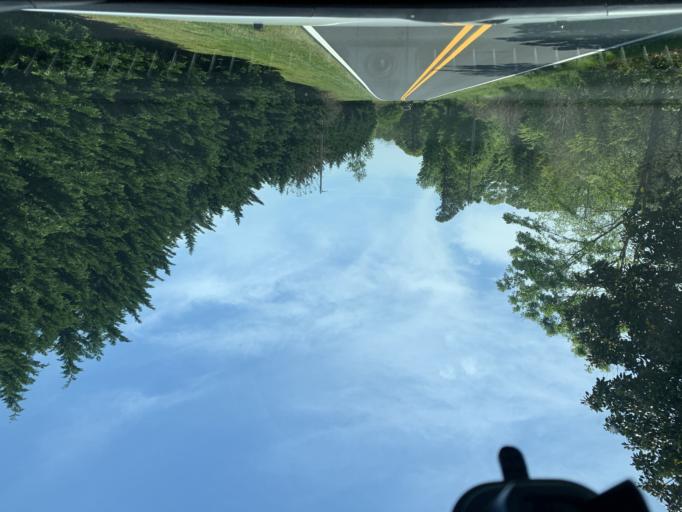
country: US
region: Georgia
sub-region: Forsyth County
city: Cumming
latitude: 34.2629
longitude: -84.0365
